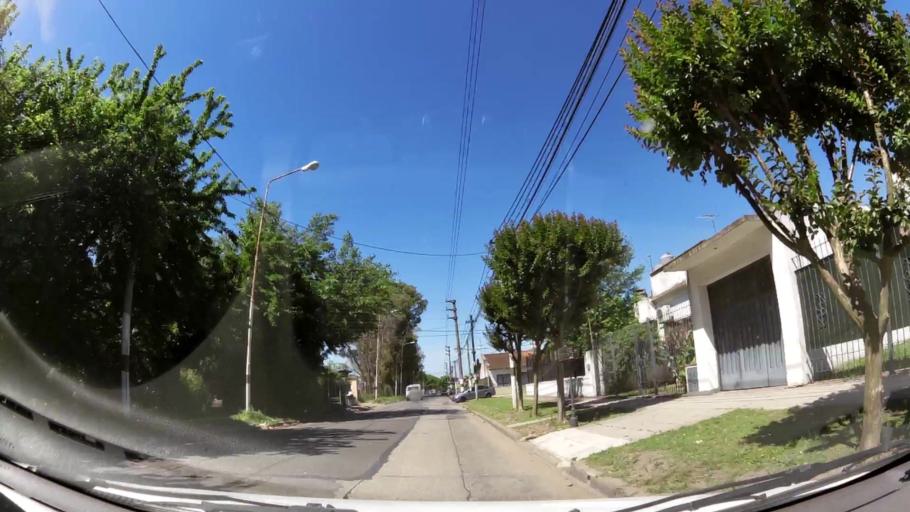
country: AR
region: Buenos Aires
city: Ituzaingo
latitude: -34.6716
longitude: -58.6613
